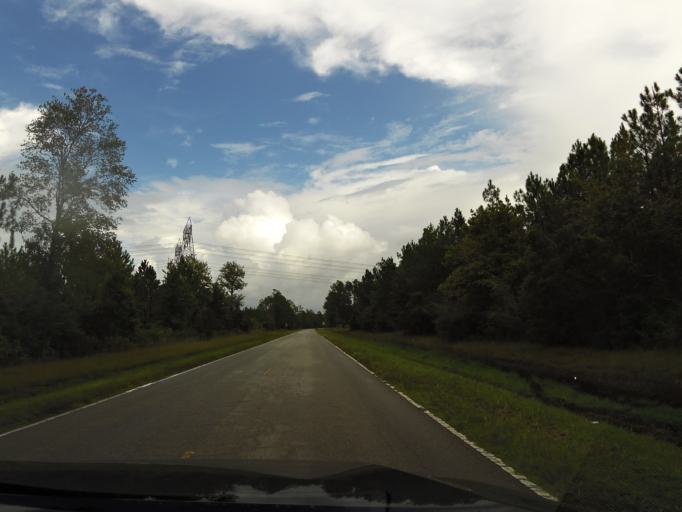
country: US
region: Florida
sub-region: Duval County
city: Baldwin
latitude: 30.3966
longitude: -81.9525
